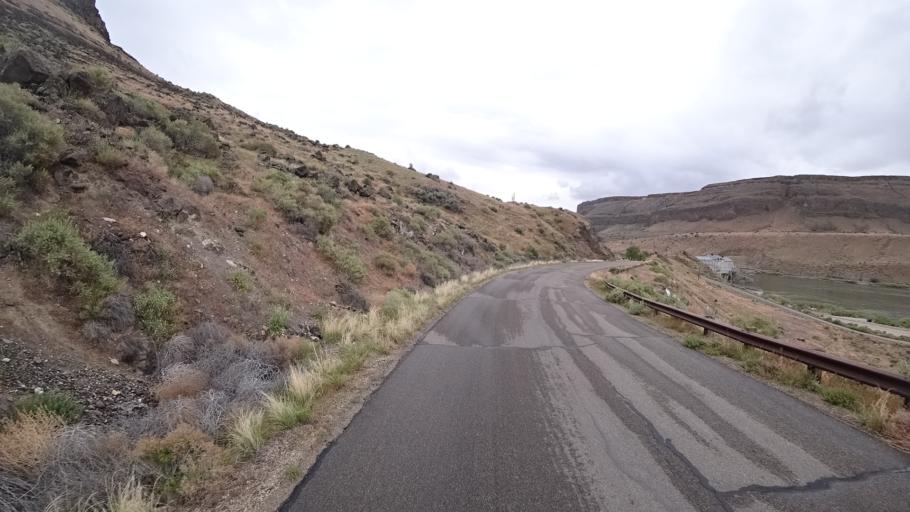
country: US
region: Idaho
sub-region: Owyhee County
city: Murphy
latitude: 43.2466
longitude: -116.3760
